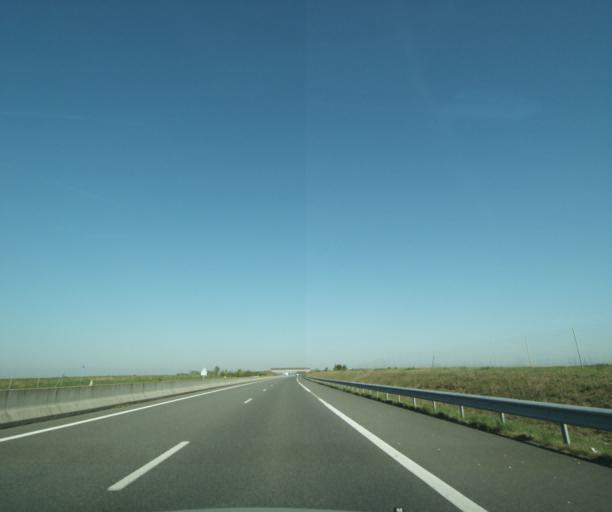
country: FR
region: Centre
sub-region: Departement du Loiret
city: Pannes
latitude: 48.0693
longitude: 2.6475
